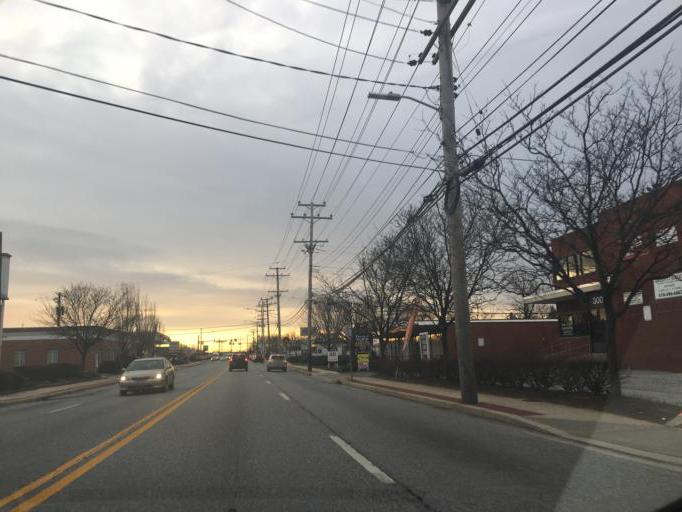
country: US
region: Maryland
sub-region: Baltimore County
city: Pikesville
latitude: 39.3664
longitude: -76.7153
